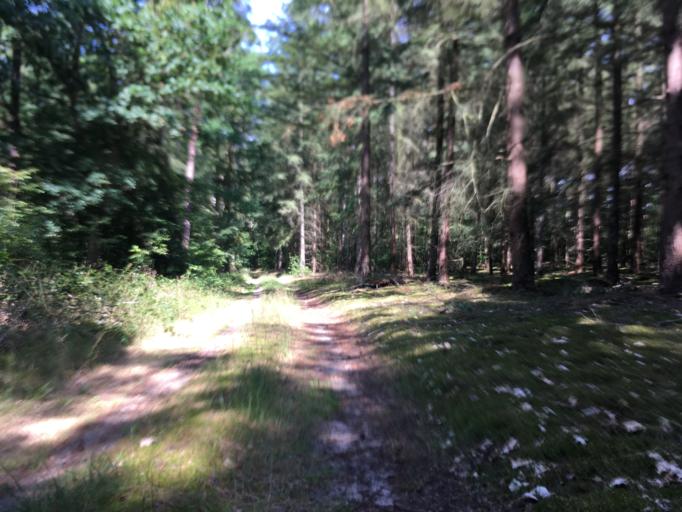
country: DE
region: Brandenburg
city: Passow
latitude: 53.2353
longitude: 14.1188
